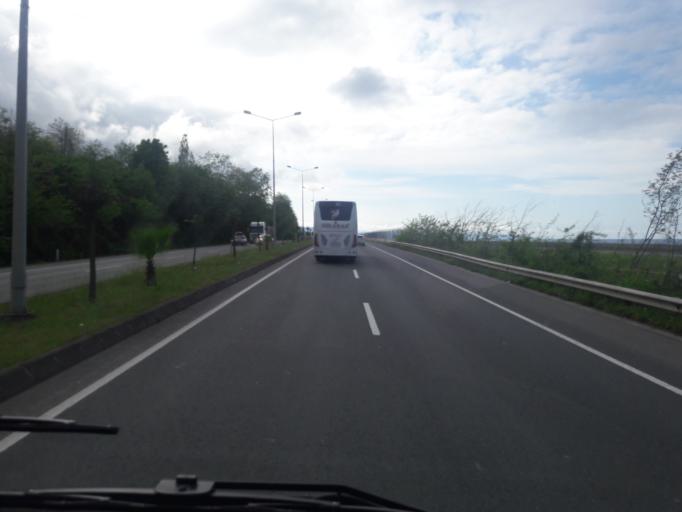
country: TR
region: Giresun
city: Piraziz
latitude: 40.9620
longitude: 38.0993
